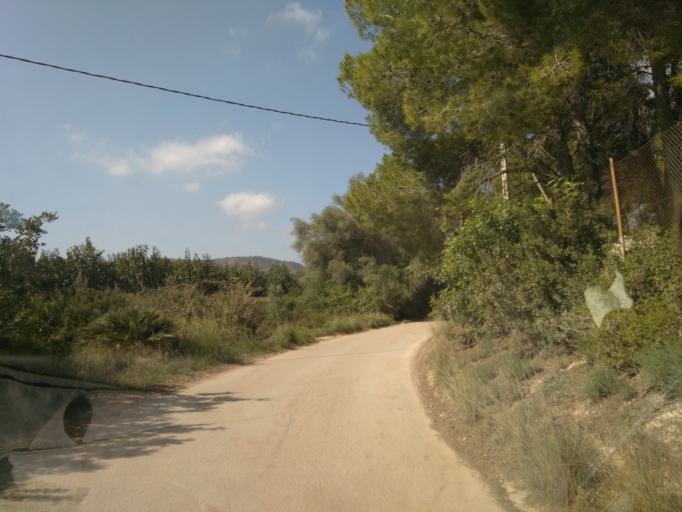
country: ES
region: Valencia
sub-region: Provincia de Valencia
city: Tous
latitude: 39.1688
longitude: -0.5879
